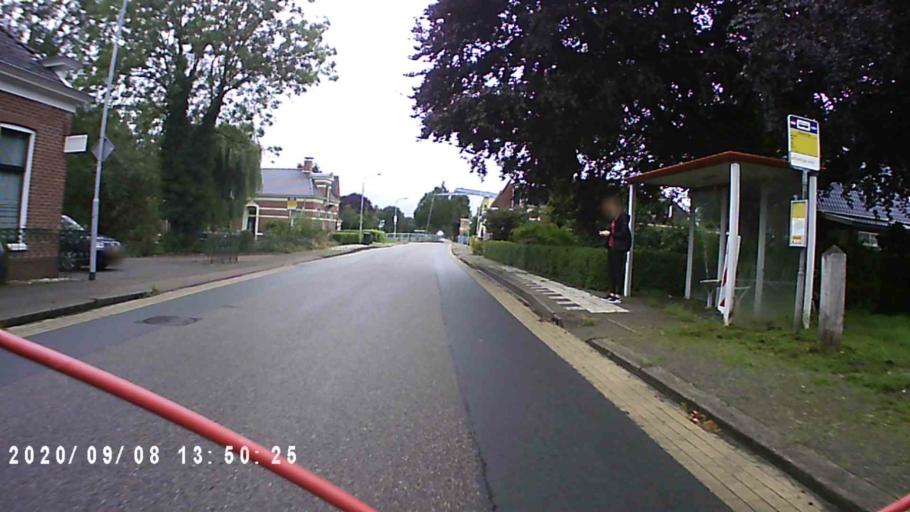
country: NL
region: Groningen
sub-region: Gemeente Veendam
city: Veendam
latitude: 53.1385
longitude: 6.8682
